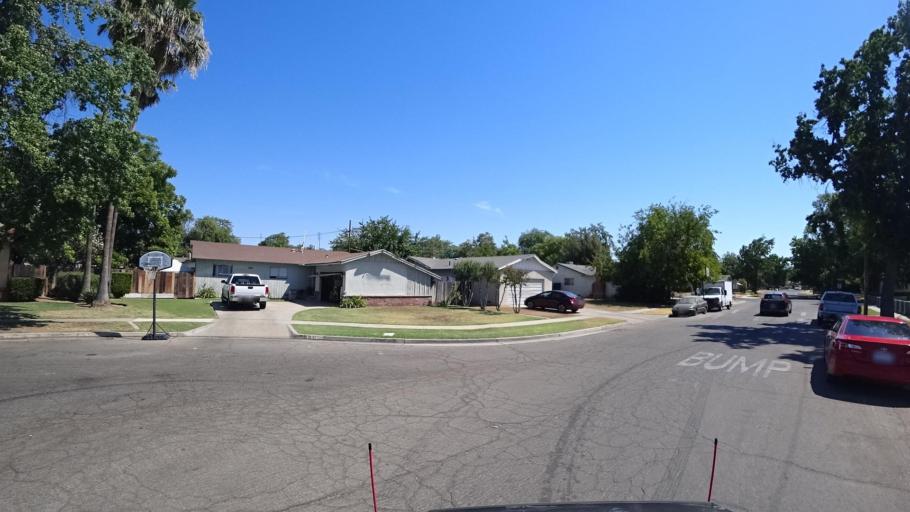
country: US
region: California
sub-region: Fresno County
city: Fresno
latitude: 36.7243
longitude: -119.7416
